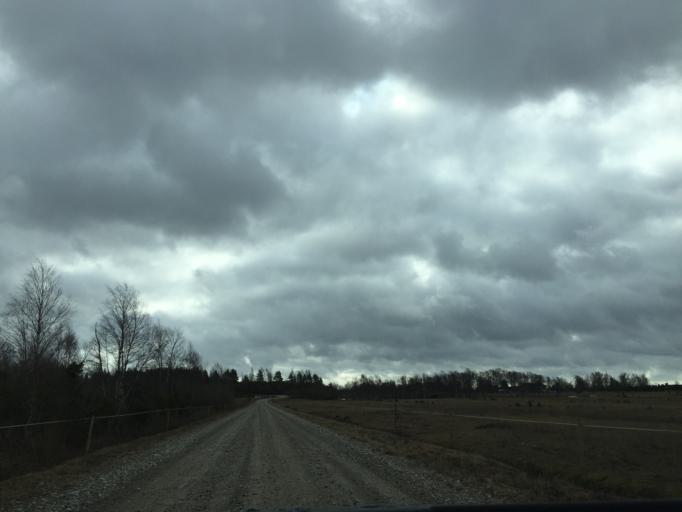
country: EE
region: Laeaene
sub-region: Haapsalu linn
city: Haapsalu
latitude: 58.6803
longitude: 23.5356
